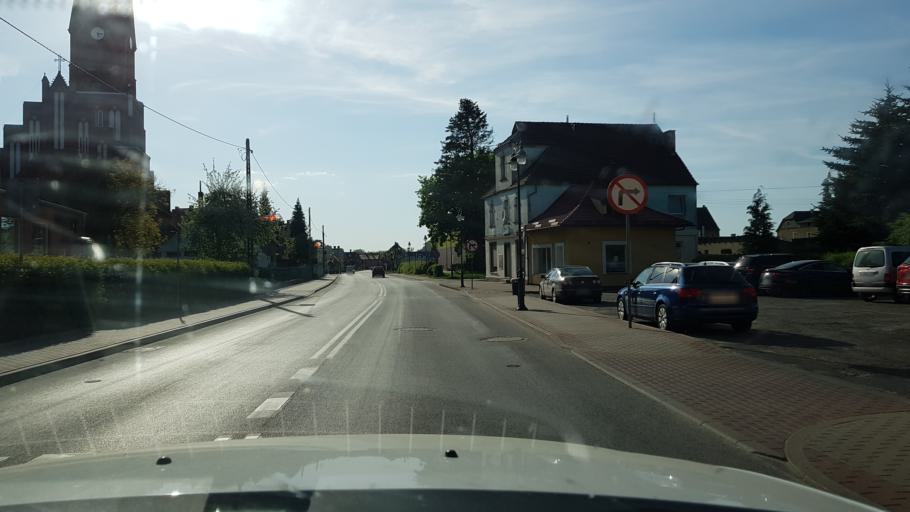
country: PL
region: West Pomeranian Voivodeship
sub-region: Powiat lobeski
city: Resko
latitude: 53.7728
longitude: 15.4085
